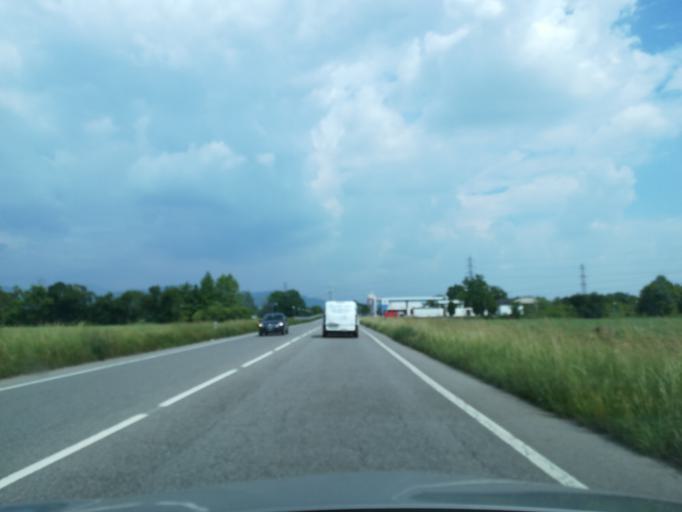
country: IT
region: Lombardy
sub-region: Provincia di Bergamo
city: Bagnatica
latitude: 45.6554
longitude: 9.7837
